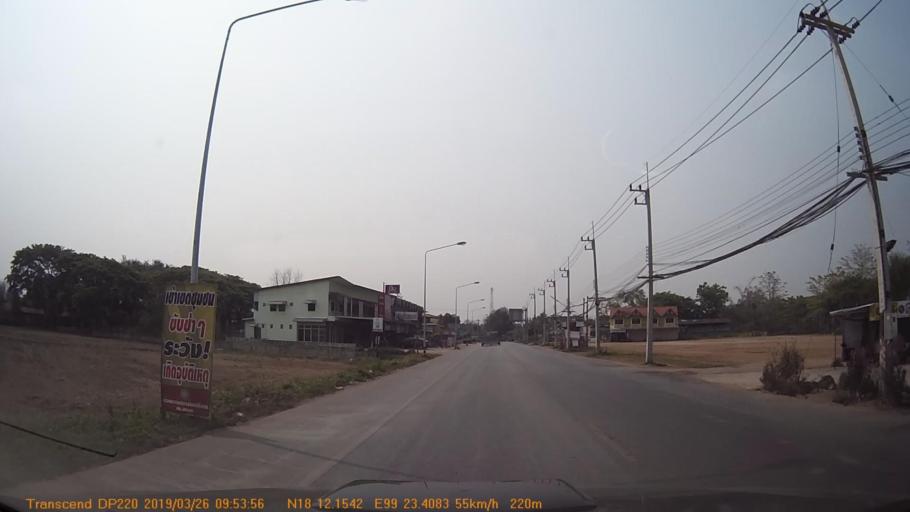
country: TH
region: Lampang
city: Ko Kha
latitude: 18.2025
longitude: 99.3902
